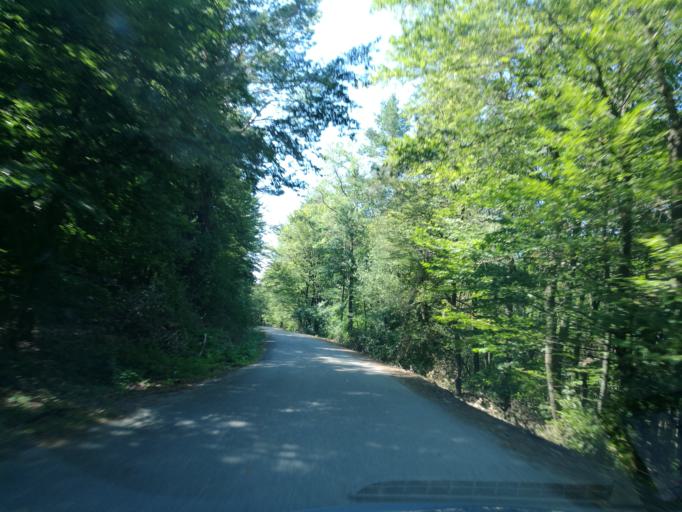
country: SK
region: Nitriansky
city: Brezova pod Bradlom
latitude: 48.6819
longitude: 17.5542
